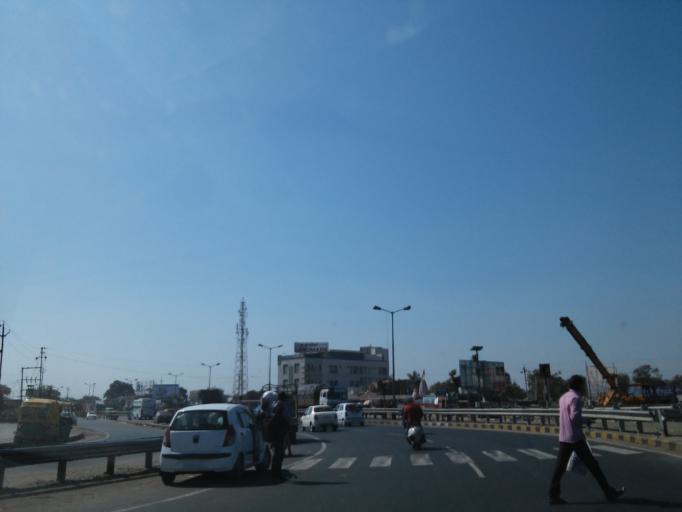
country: IN
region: Gujarat
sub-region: Sabar Kantha
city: Himatnagar
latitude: 23.5809
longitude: 72.9593
